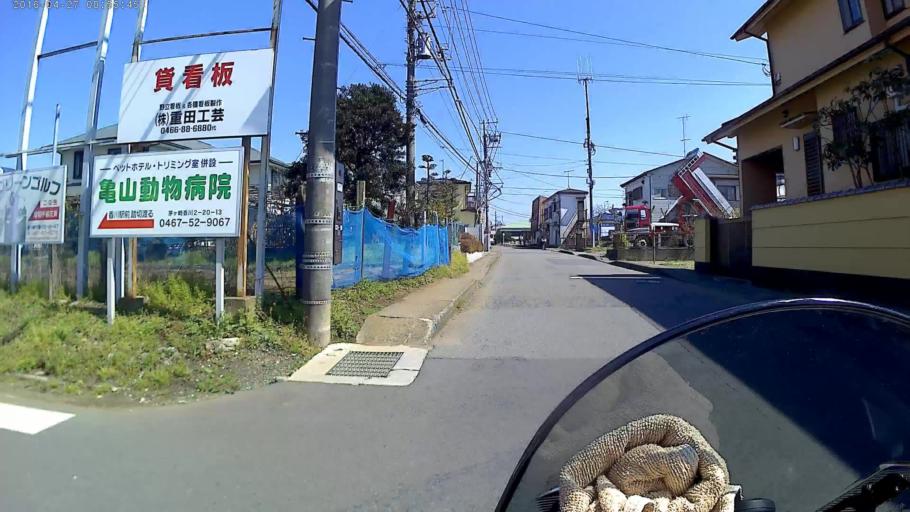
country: JP
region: Kanagawa
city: Chigasaki
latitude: 35.3513
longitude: 139.3991
